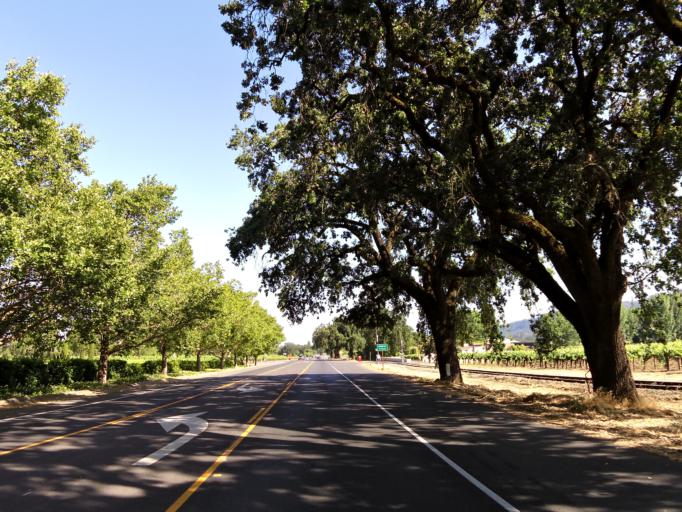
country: US
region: California
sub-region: Napa County
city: Saint Helena
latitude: 38.4741
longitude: -122.4339
